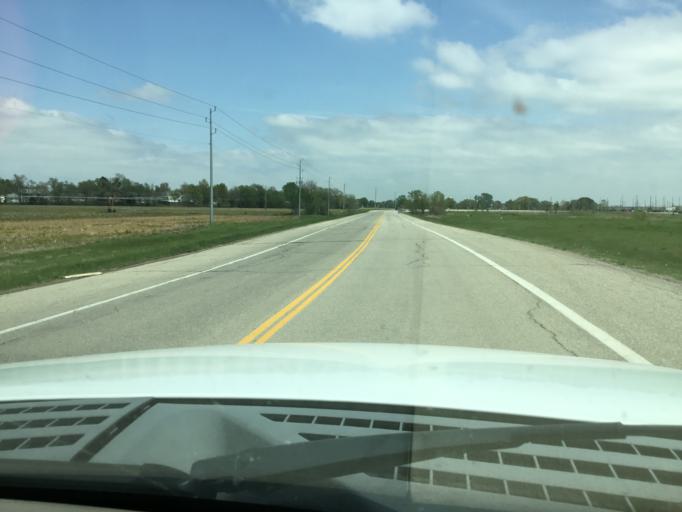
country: US
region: Kansas
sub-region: Osage County
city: Carbondale
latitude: 38.9321
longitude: -95.7004
